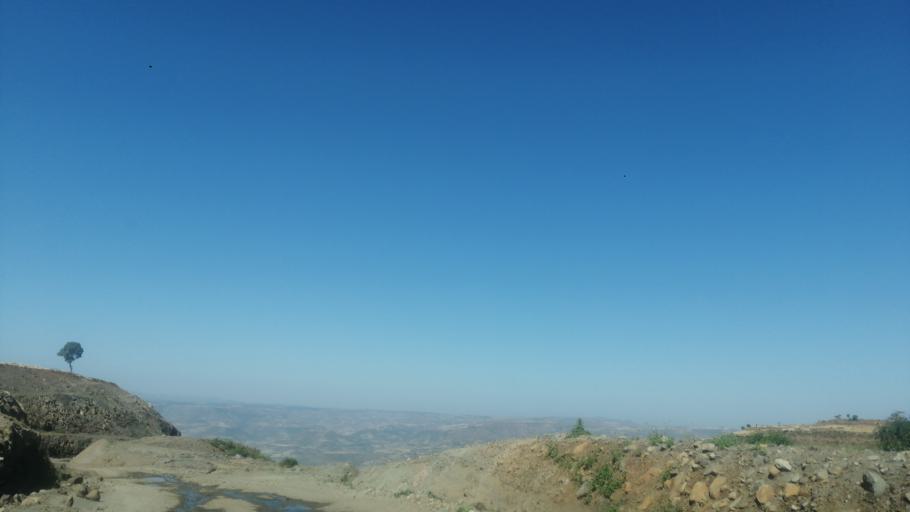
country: ET
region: Amhara
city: Addiet Canna
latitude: 11.1523
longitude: 37.8602
